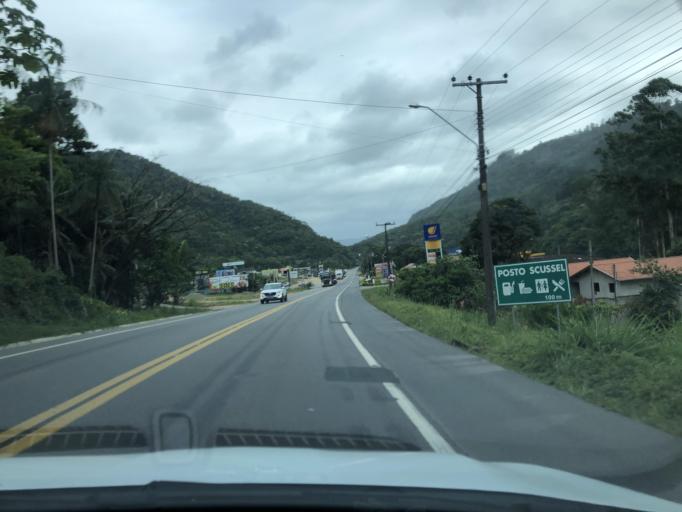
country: BR
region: Santa Catarina
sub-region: Ibirama
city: Ibirama
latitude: -27.0791
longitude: -49.4867
